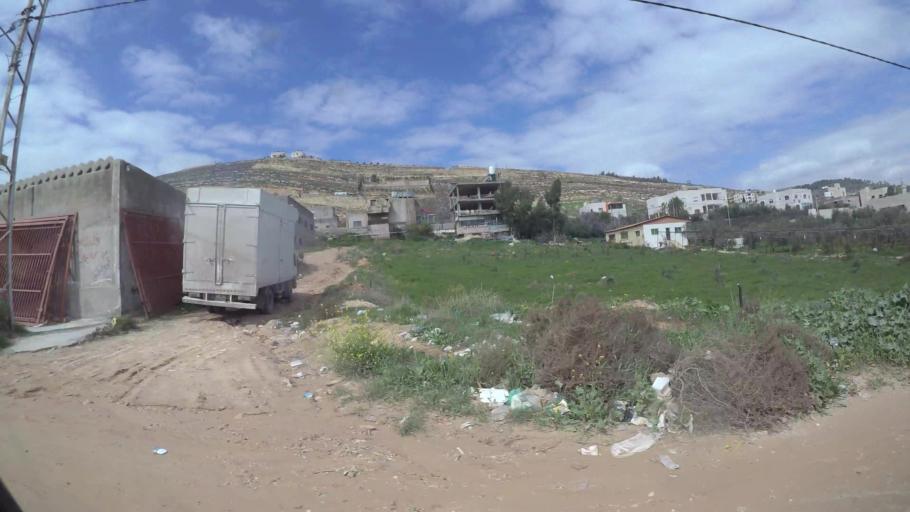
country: JO
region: Amman
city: Al Jubayhah
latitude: 32.0664
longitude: 35.8129
